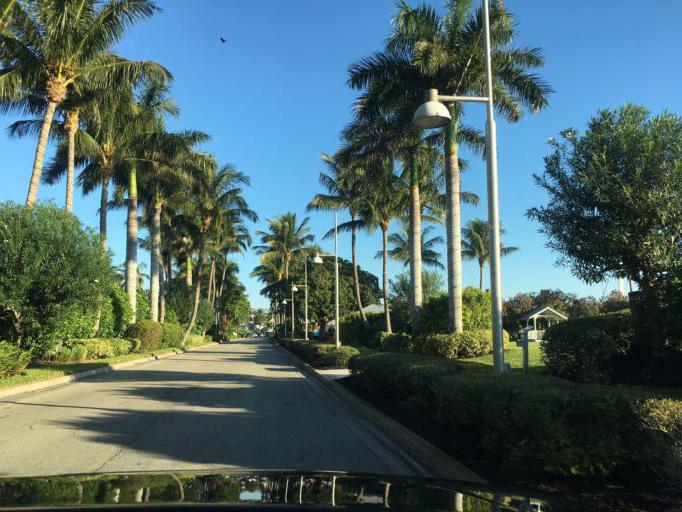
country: US
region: Florida
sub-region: Lee County
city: Pine Island Center
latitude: 26.5467
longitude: -82.1975
